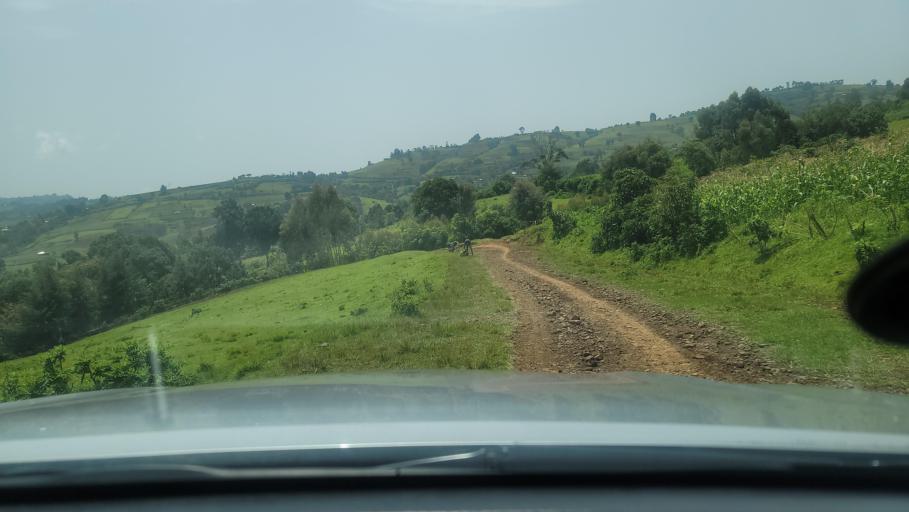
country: ET
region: Oromiya
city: Agaro
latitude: 7.8395
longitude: 36.4080
